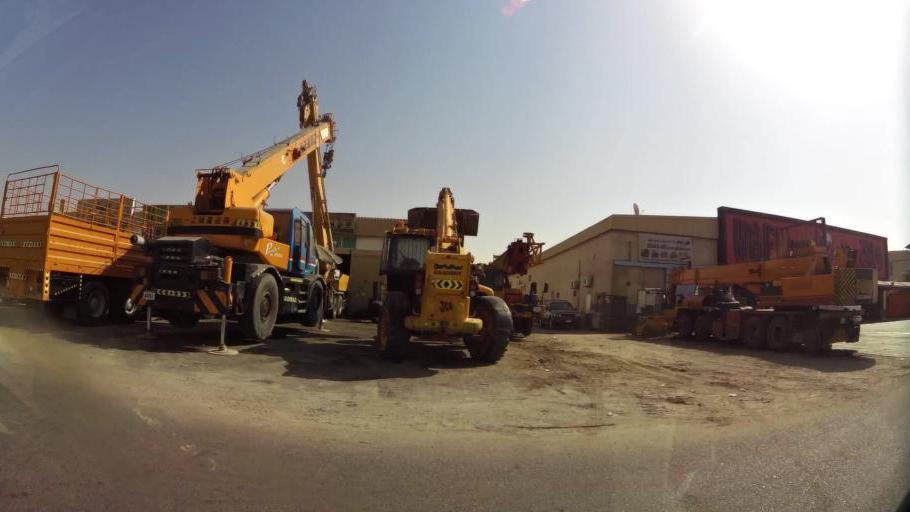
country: AE
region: Ajman
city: Ajman
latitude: 25.4287
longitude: 55.5202
